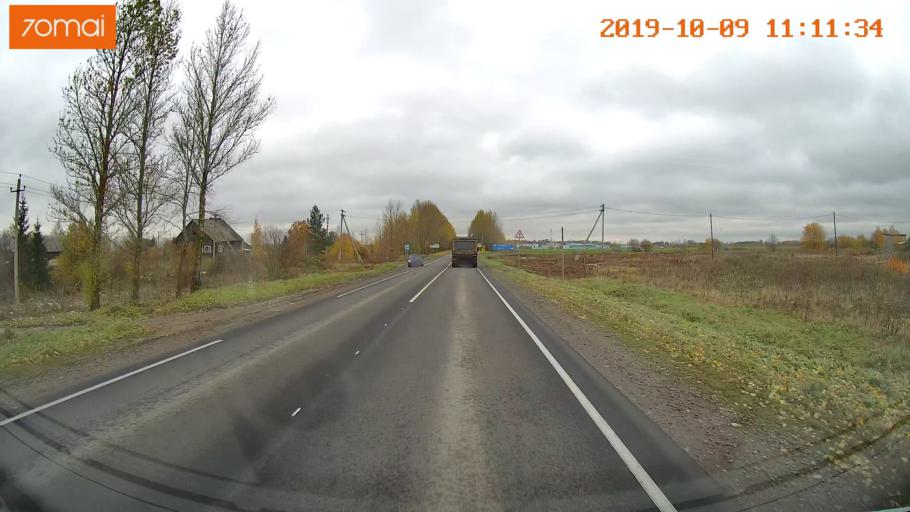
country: RU
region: Vologda
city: Vologda
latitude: 59.1693
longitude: 39.8218
